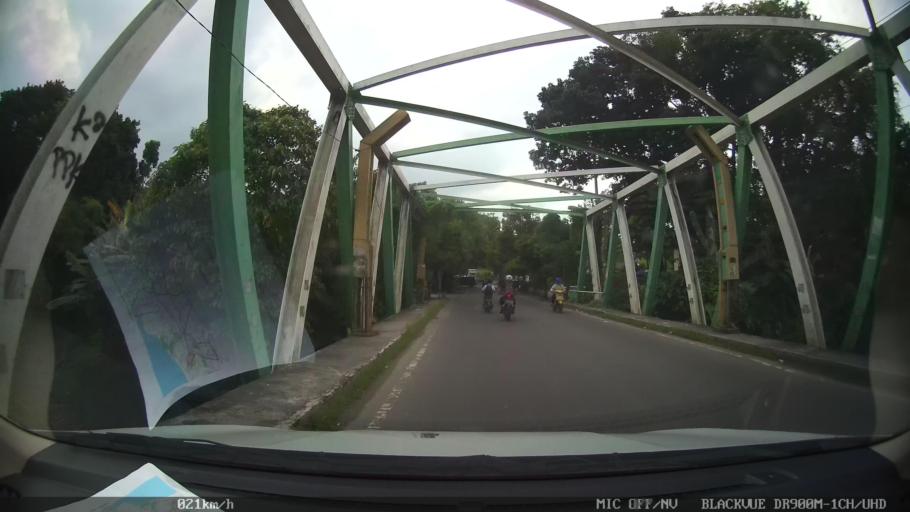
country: ID
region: North Sumatra
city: Medan
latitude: 3.5578
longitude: 98.6834
